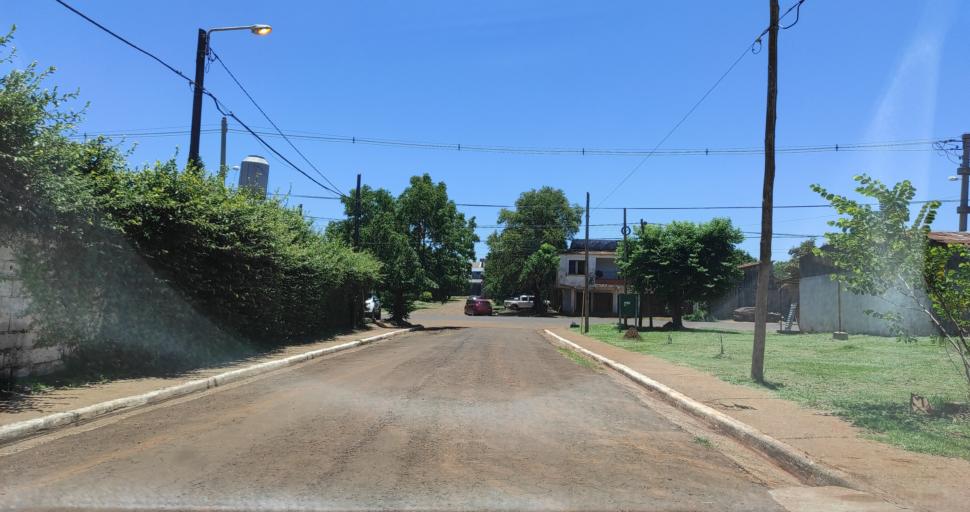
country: AR
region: Misiones
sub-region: Departamento de Capital
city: Posadas
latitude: -27.4064
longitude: -55.9072
